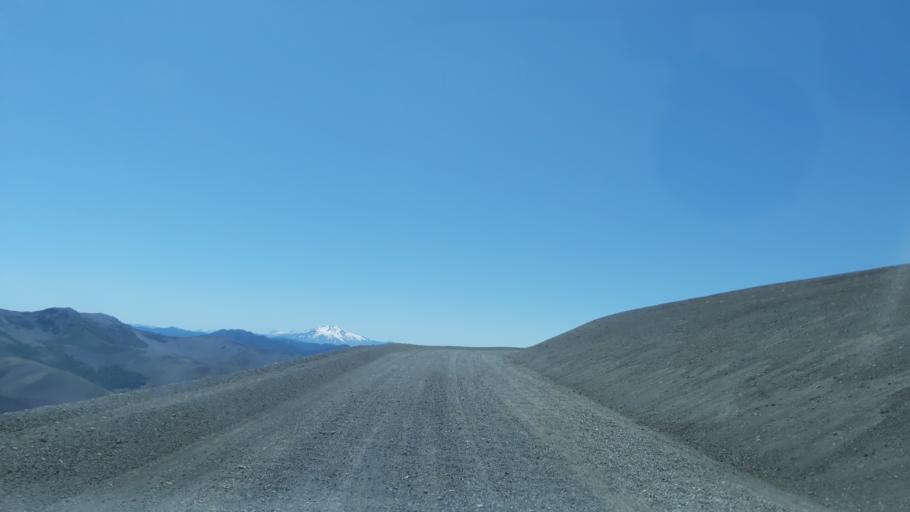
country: CL
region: Araucania
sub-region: Provincia de Cautin
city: Vilcun
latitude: -38.3679
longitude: -71.5399
